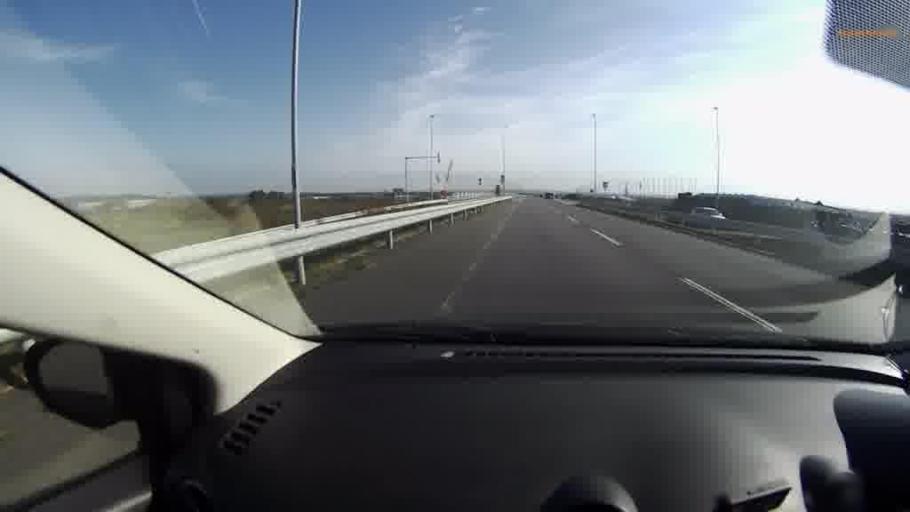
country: JP
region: Hokkaido
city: Kushiro
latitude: 43.0353
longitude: 144.3158
